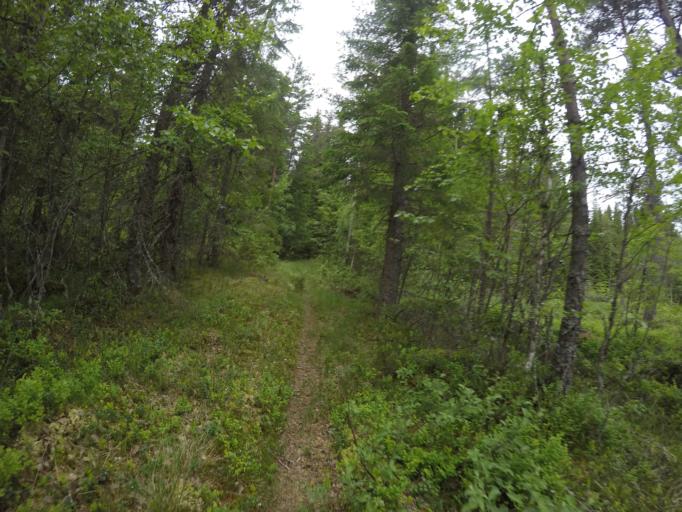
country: SE
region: Dalarna
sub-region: Ludvika Kommun
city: Abborrberget
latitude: 60.0720
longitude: 14.5270
